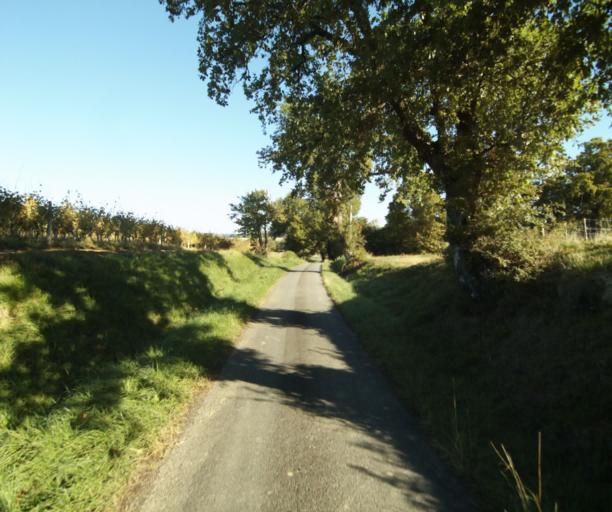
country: FR
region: Midi-Pyrenees
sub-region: Departement du Gers
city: Gondrin
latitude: 43.8426
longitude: 0.2327
